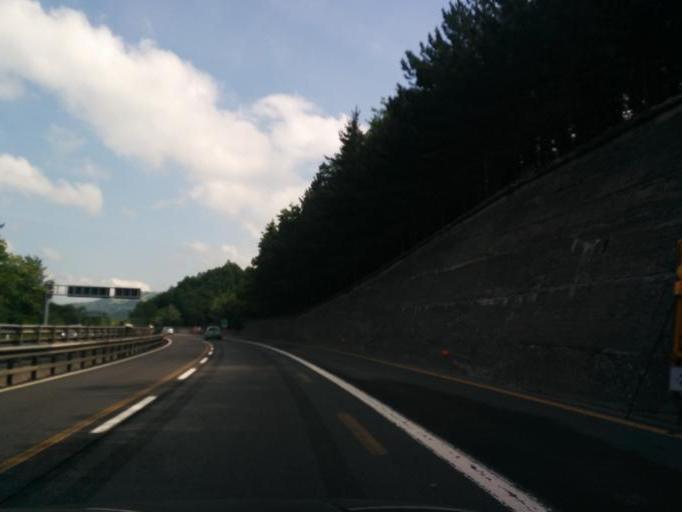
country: IT
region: Emilia-Romagna
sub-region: Provincia di Bologna
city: Castiglione dei Pepoli
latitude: 44.1609
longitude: 11.2084
